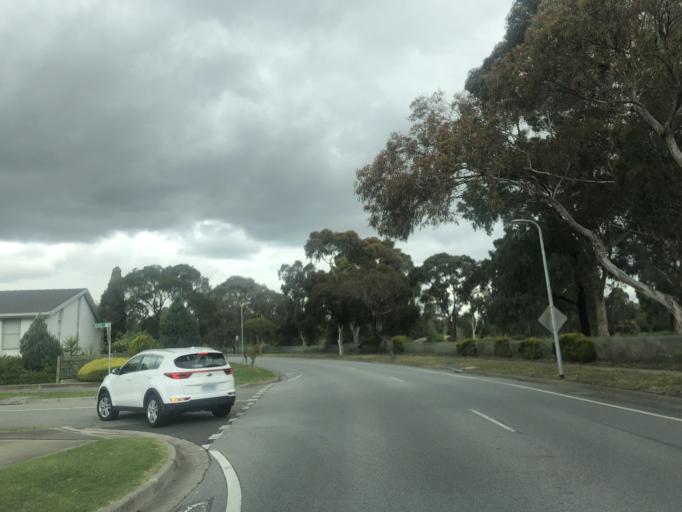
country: AU
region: Victoria
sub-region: Casey
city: Endeavour Hills
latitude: -37.9773
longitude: 145.2434
